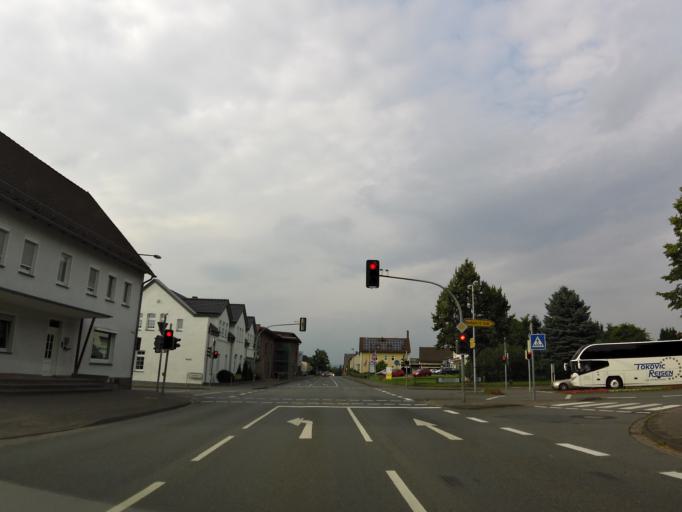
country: DE
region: Lower Saxony
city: Boffzen
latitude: 51.7501
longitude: 9.3986
